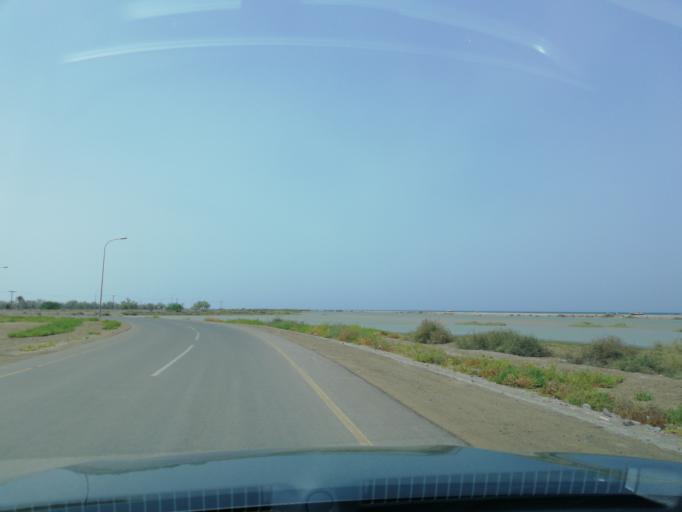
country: OM
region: Al Batinah
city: Shinas
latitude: 24.7525
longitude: 56.4673
